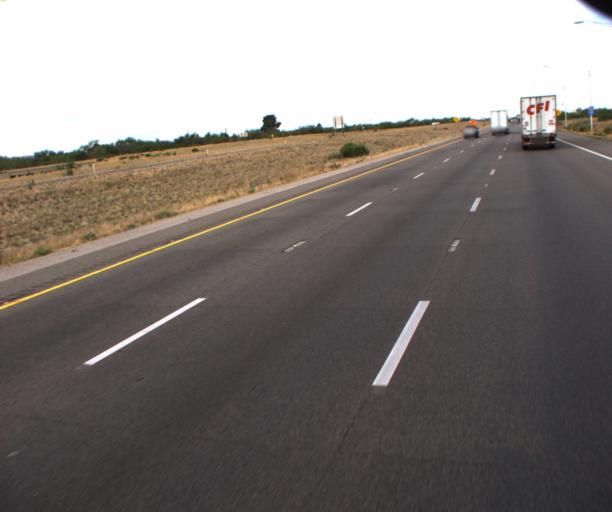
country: US
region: Arizona
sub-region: Cochise County
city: Whetstone
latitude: 31.9635
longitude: -110.3597
